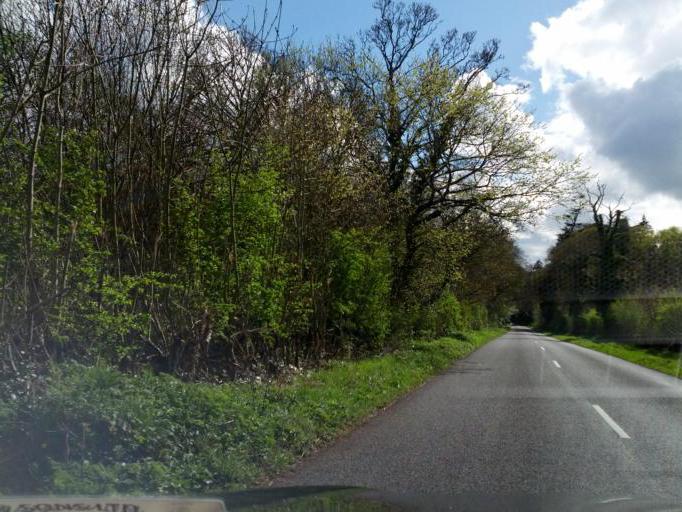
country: IE
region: Leinster
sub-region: An Mhi
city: Dunshaughlin
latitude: 53.5360
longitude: -6.6303
